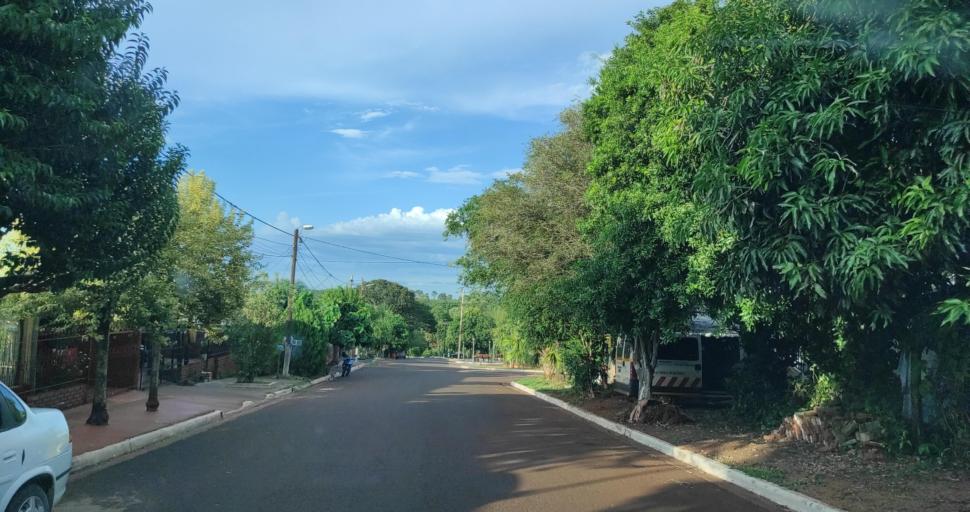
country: AR
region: Misiones
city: Santo Pipo
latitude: -27.1396
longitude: -55.4114
